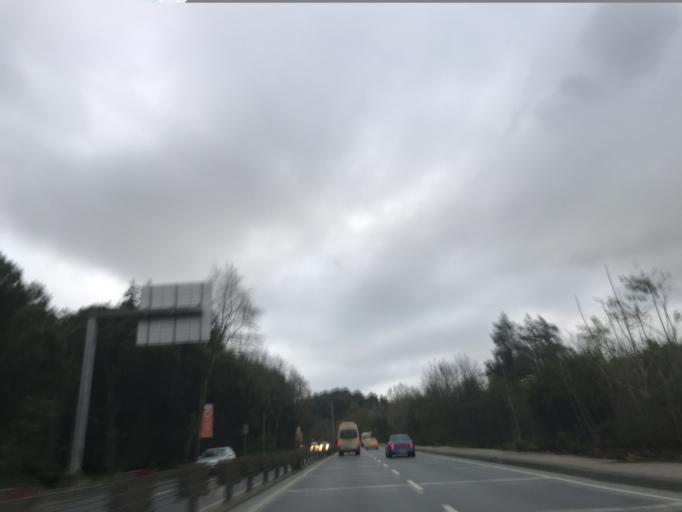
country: TR
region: Istanbul
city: Arikoey
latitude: 41.1491
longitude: 29.0289
